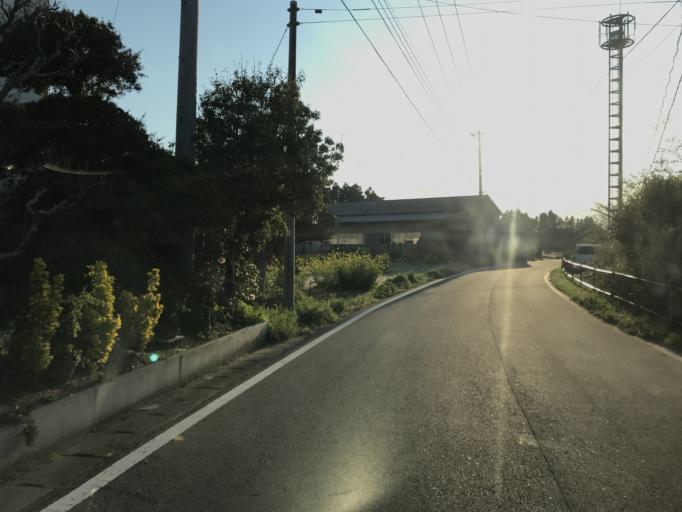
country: JP
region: Chiba
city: Yokaichiba
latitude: 35.7708
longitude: 140.5378
